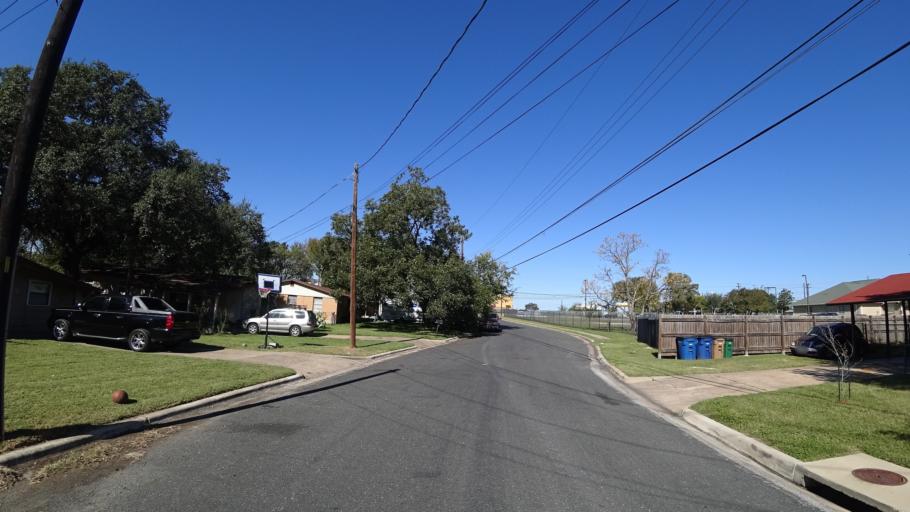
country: US
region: Texas
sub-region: Travis County
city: Austin
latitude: 30.2844
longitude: -97.6825
